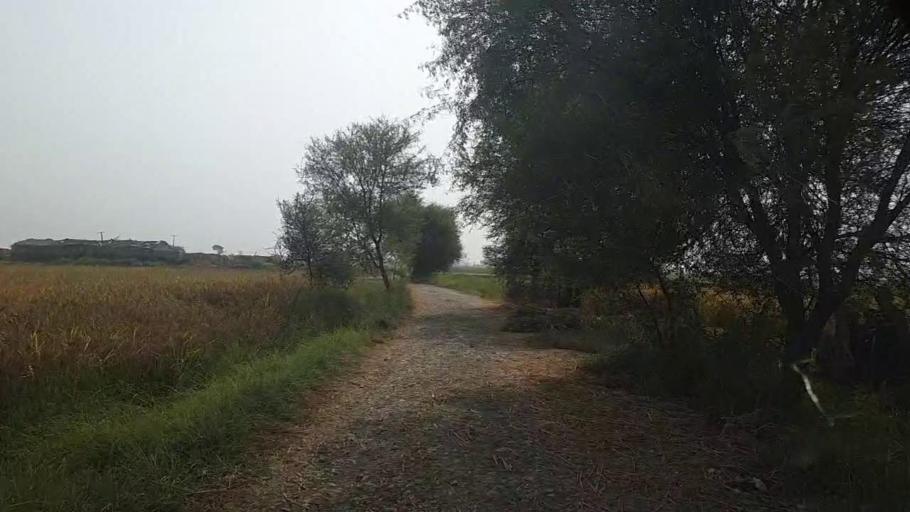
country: PK
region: Sindh
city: Kashmor
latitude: 28.3876
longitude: 69.4272
